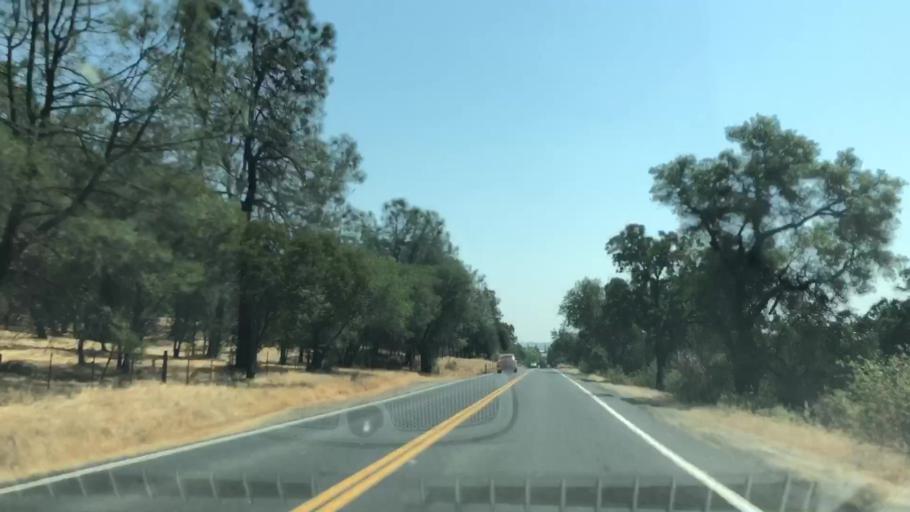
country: US
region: California
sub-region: Calaveras County
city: Copperopolis
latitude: 37.9458
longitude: -120.6087
